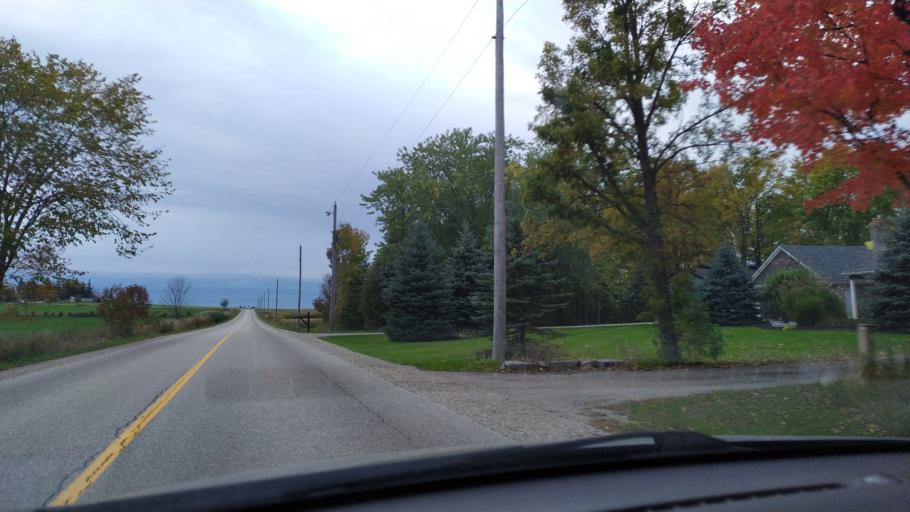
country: CA
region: Ontario
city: Waterloo
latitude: 43.5131
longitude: -80.7475
